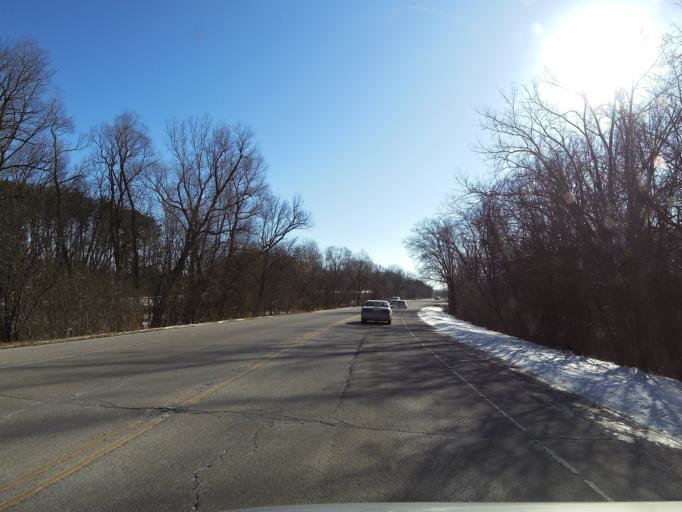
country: US
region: Minnesota
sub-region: Ramsey County
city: Maplewood
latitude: 44.9328
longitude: -92.9964
